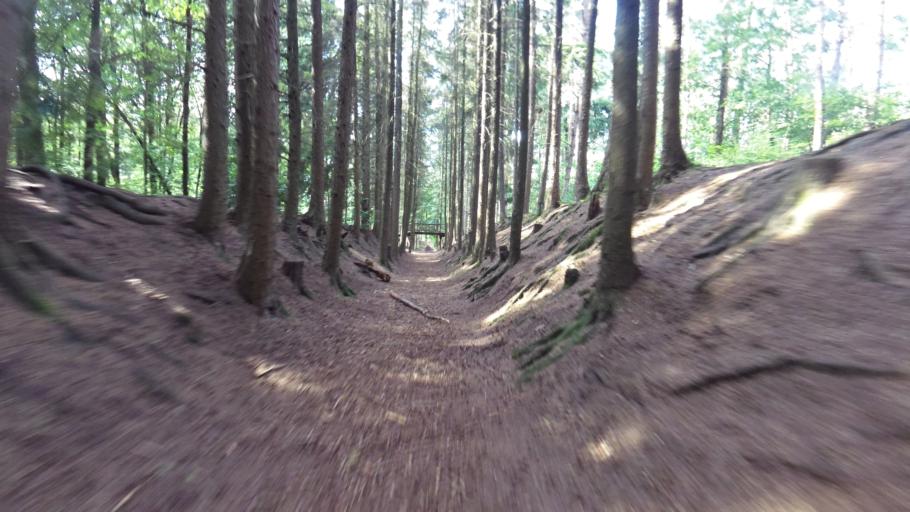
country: NL
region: Gelderland
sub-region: Gemeente Renkum
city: Doorwerth
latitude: 51.9940
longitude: 5.8167
